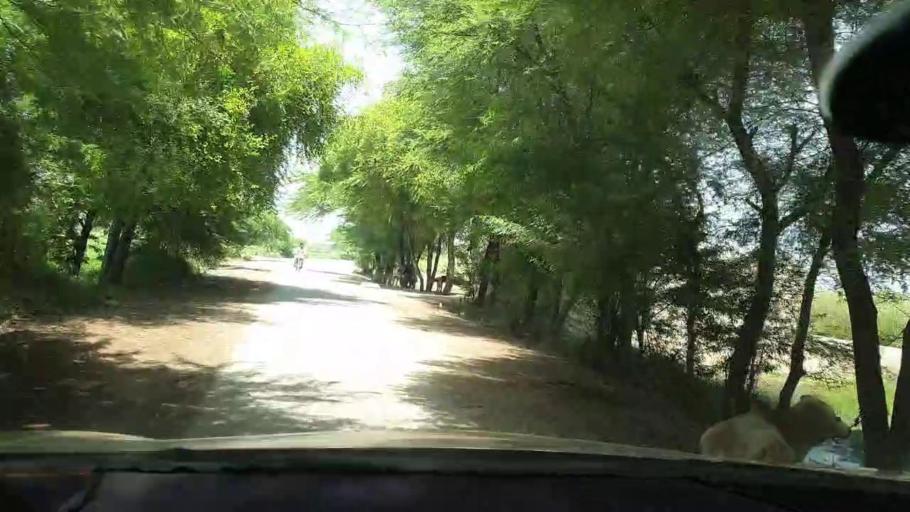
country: PK
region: Sindh
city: Kambar
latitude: 27.6676
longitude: 67.9139
